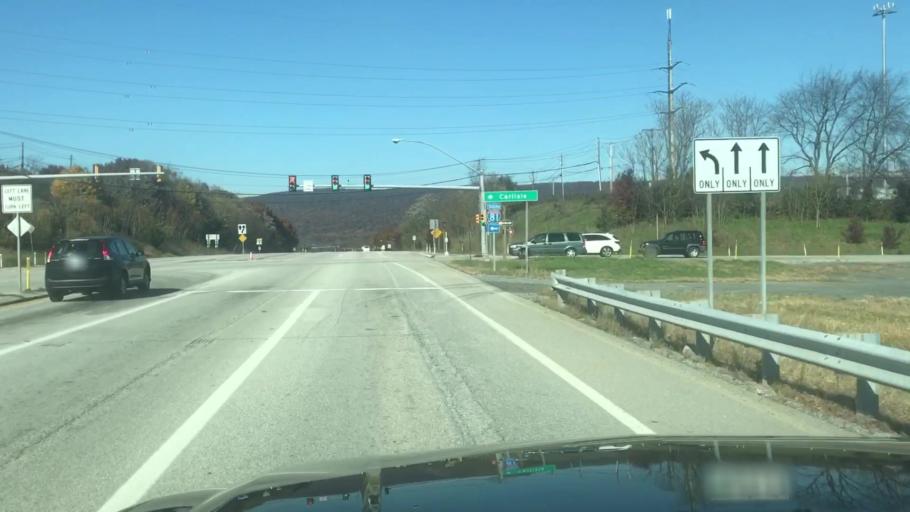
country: US
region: Pennsylvania
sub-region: Cumberland County
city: Mechanicsburg
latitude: 40.2698
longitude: -77.0442
